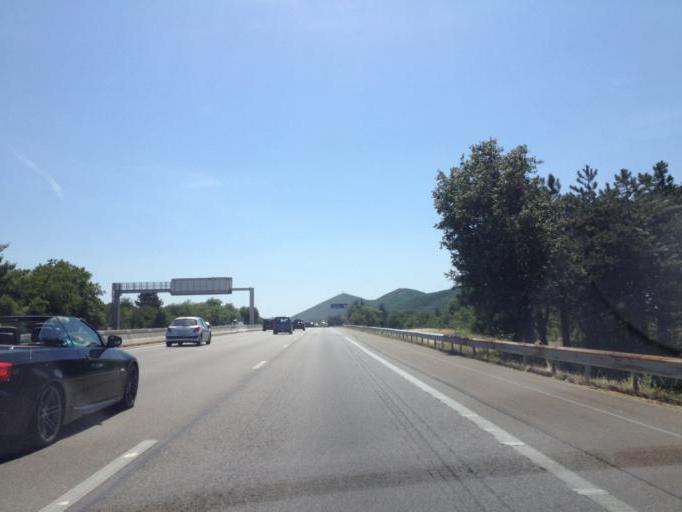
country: FR
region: Rhone-Alpes
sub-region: Departement de l'Ardeche
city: Cruas
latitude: 44.6521
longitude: 4.7941
